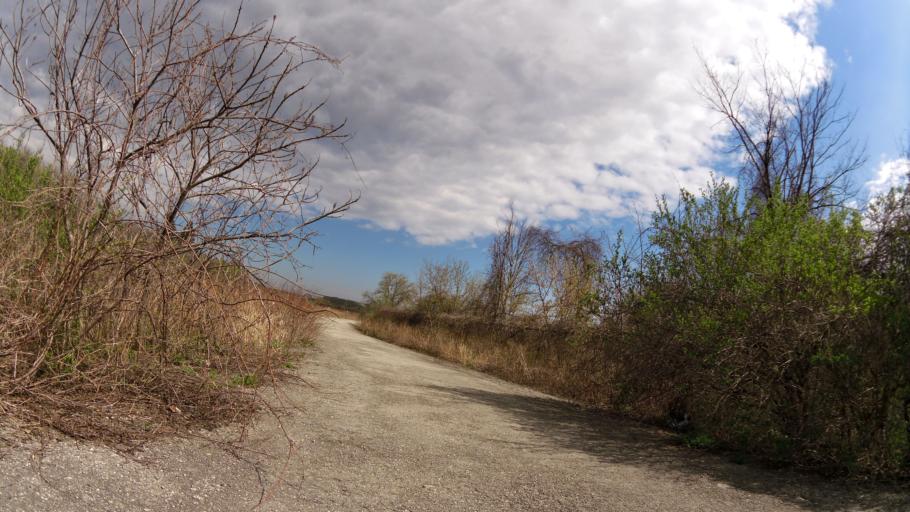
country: CA
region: Ontario
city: Etobicoke
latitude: 43.6730
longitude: -79.6448
